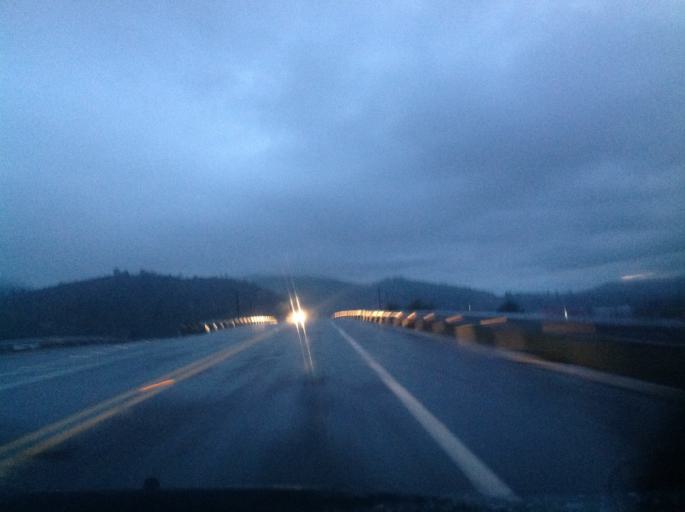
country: MX
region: Puebla
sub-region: Oriental
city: San Antonio Virreyes
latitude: 19.4194
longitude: -97.6393
